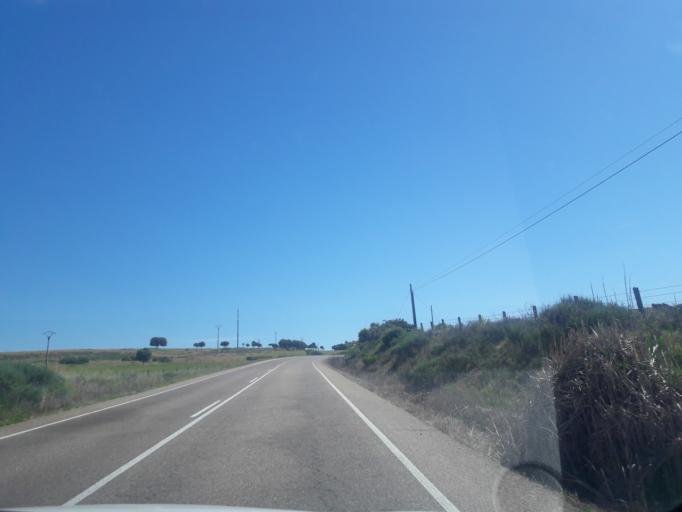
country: ES
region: Castille and Leon
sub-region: Provincia de Salamanca
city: Cerralbo
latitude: 40.9785
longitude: -6.5771
